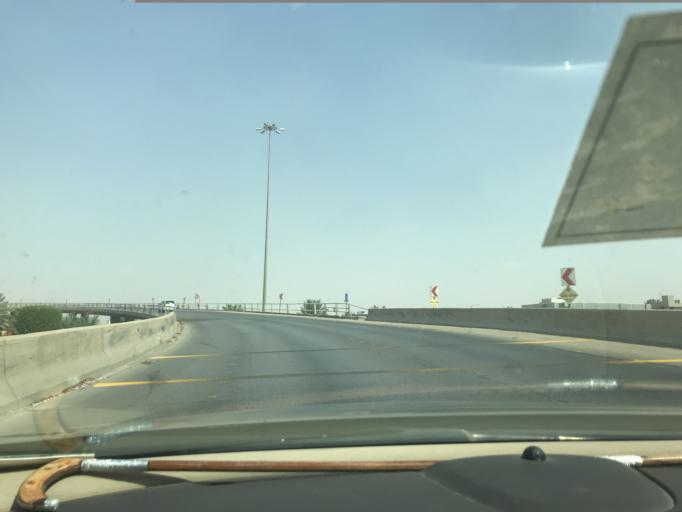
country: SA
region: Ar Riyad
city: Riyadh
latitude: 24.7128
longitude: 46.7615
